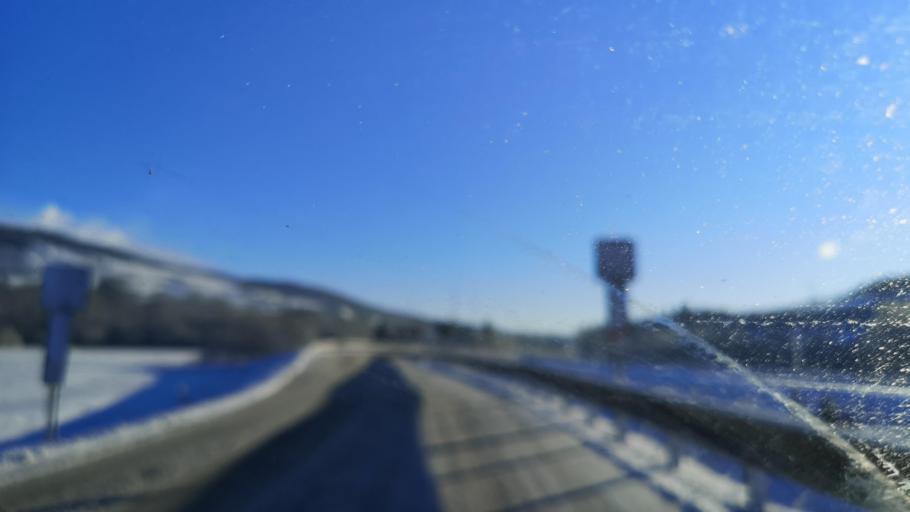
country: SK
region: Banskobystricky
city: Tisovec
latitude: 48.8522
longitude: 20.0048
